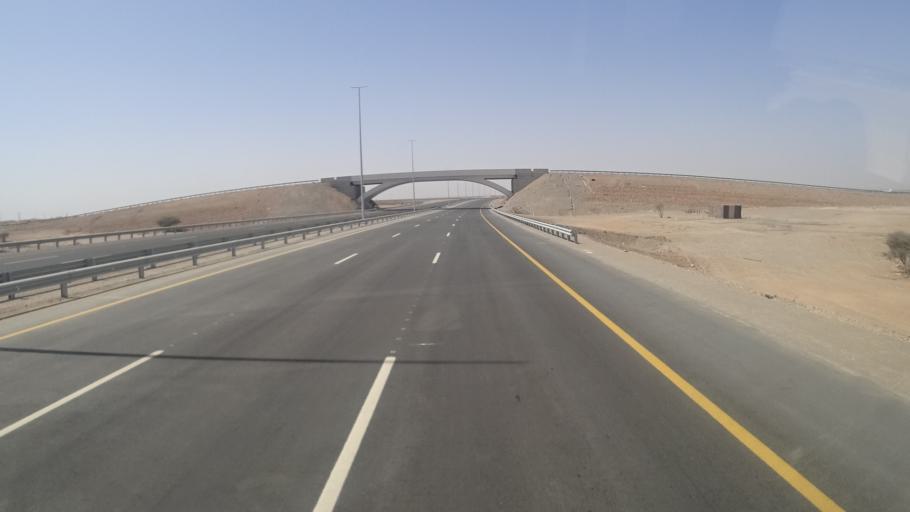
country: OM
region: Ash Sharqiyah
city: Sur
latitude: 22.2805
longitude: 59.2670
